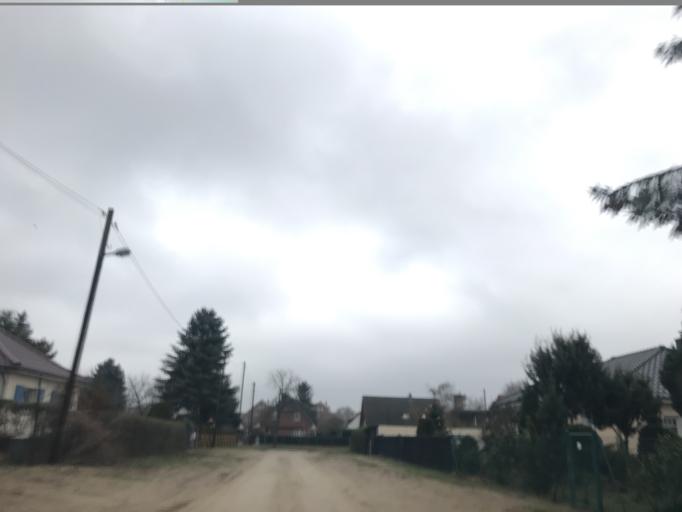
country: DE
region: Brandenburg
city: Falkensee
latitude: 52.5610
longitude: 13.1123
